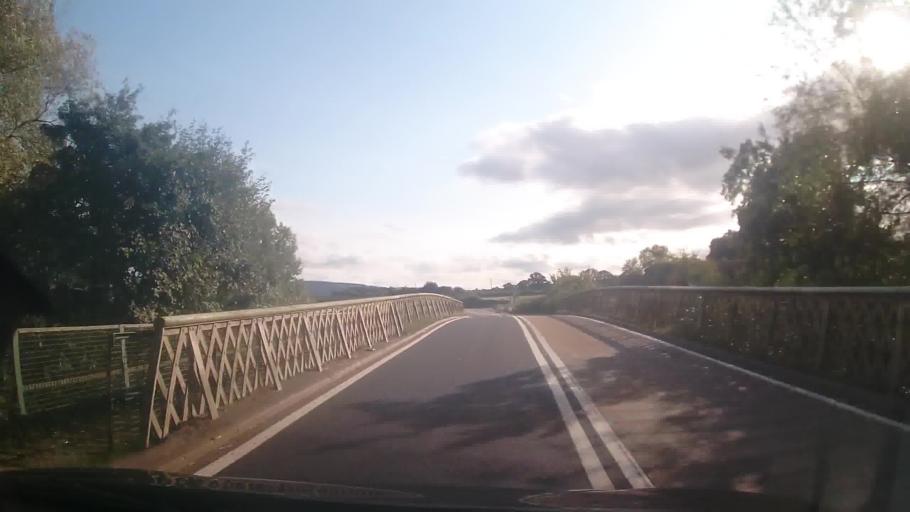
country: GB
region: England
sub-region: Shropshire
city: Bromfield
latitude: 52.4068
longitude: -2.8038
